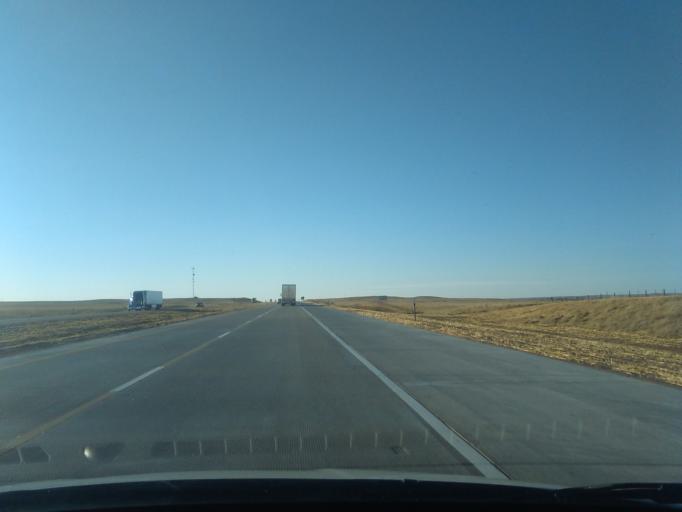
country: US
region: Nebraska
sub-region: Deuel County
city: Chappell
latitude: 41.1136
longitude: -102.5961
